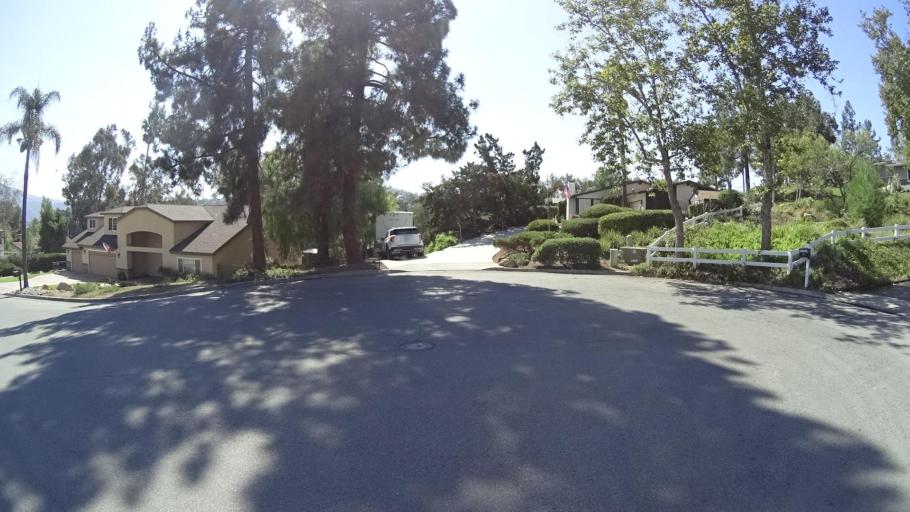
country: US
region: California
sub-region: San Diego County
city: Granite Hills
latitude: 32.7874
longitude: -116.8936
